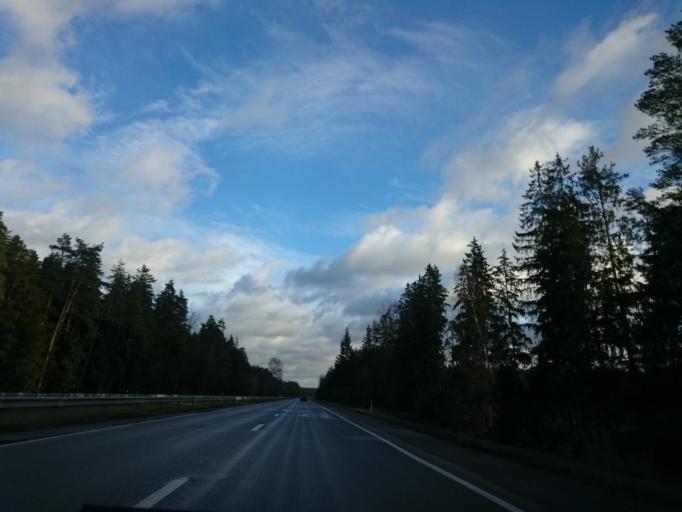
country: LV
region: Krimulda
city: Ragana
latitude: 57.1317
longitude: 24.7462
